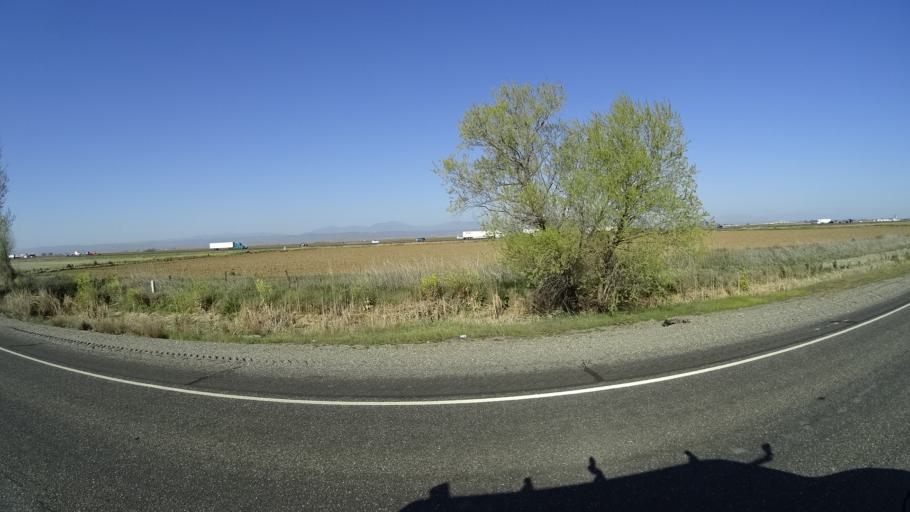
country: US
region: California
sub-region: Glenn County
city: Willows
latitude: 39.4809
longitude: -122.1931
